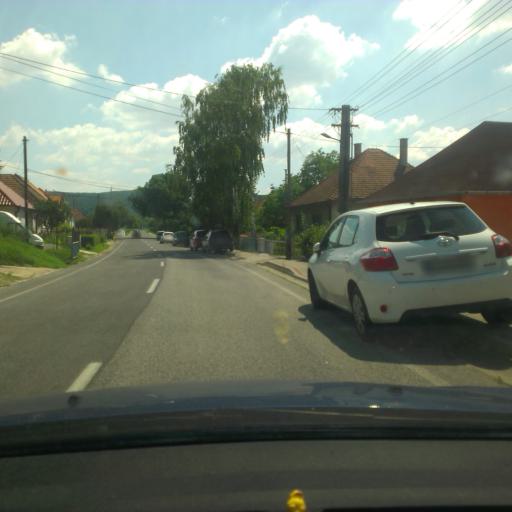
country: SK
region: Trnavsky
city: Hlohovec
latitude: 48.4716
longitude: 17.8096
